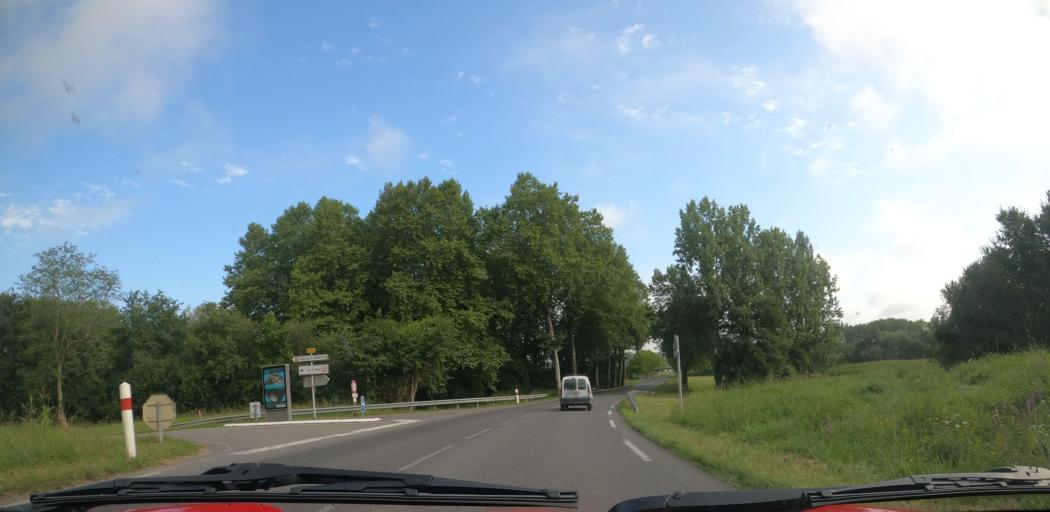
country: FR
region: Aquitaine
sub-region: Departement des Landes
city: Peyrehorade
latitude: 43.5321
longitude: -1.1102
